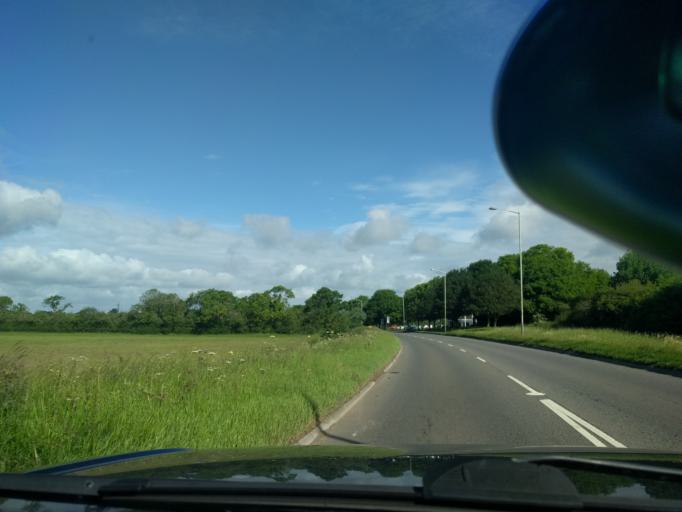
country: GB
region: England
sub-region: Wiltshire
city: Bremhill
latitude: 51.4431
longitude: -2.0780
